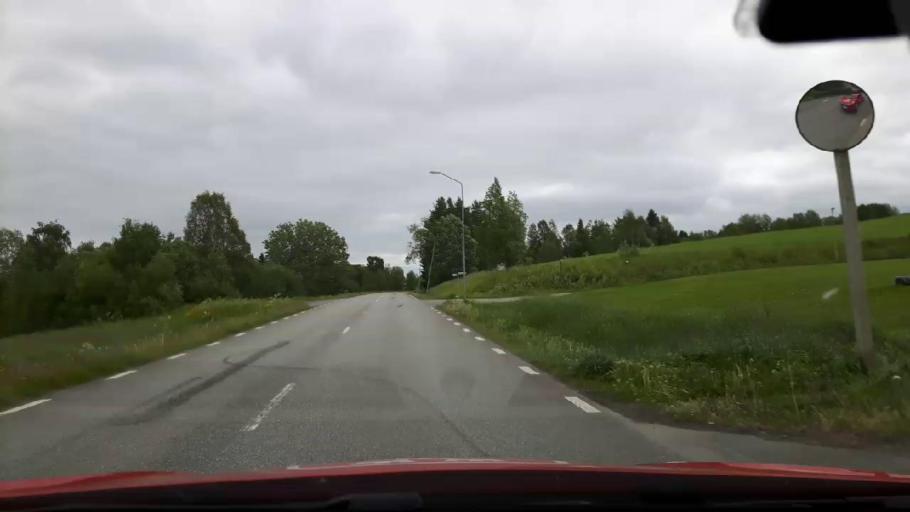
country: SE
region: Jaemtland
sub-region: Stroemsunds Kommun
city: Stroemsund
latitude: 63.5768
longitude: 15.3717
